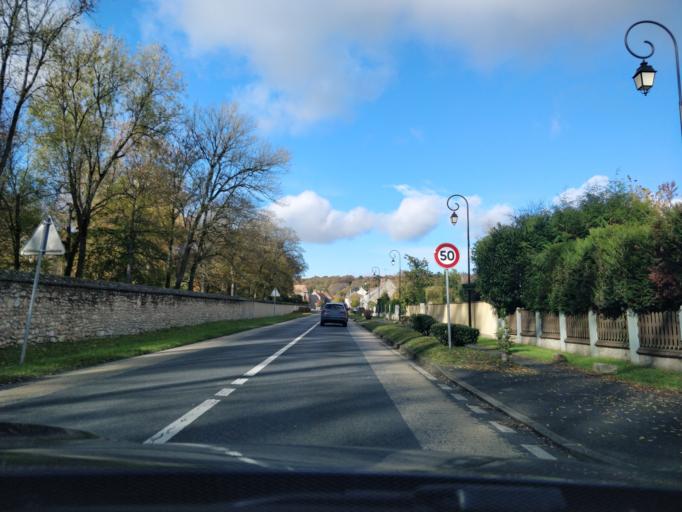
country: FR
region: Ile-de-France
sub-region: Departement de l'Essonne
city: Fontenay-les-Briis
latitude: 48.6171
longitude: 2.1586
